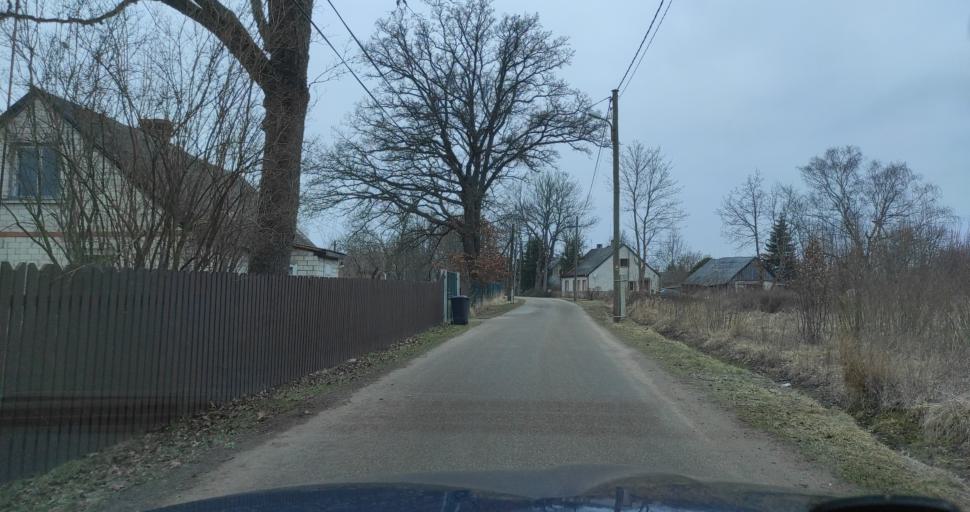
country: LV
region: Ventspils Rajons
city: Piltene
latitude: 57.2240
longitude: 21.6845
